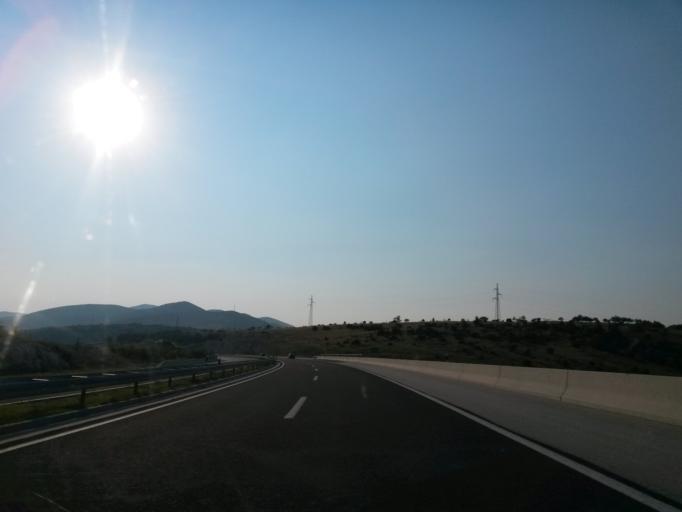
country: HR
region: Splitsko-Dalmatinska
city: Dugopolje
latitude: 43.6019
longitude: 16.6215
